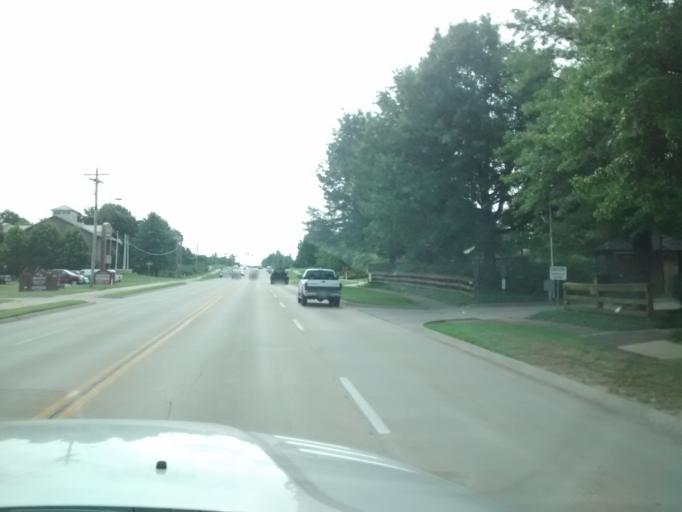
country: US
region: Arkansas
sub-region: Washington County
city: Johnson
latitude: 36.1201
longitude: -94.1333
